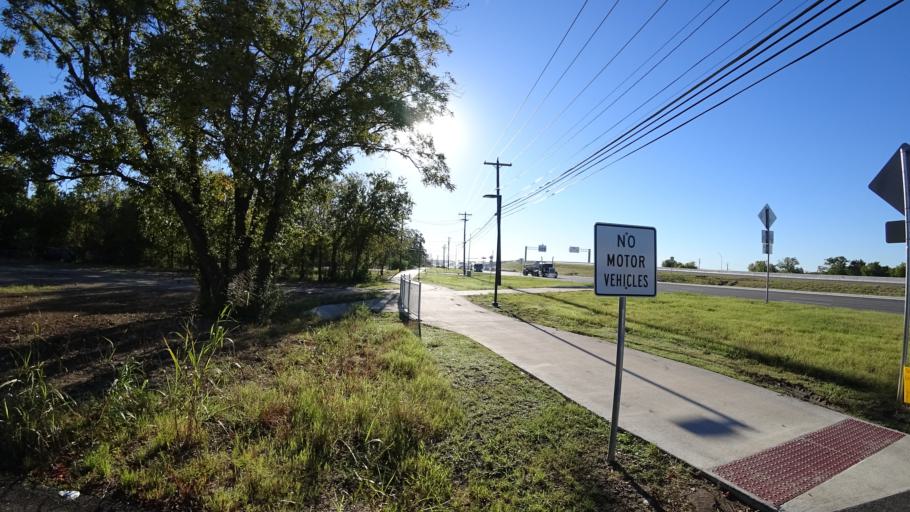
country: US
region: Texas
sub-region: Travis County
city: Hornsby Bend
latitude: 30.2048
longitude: -97.6419
